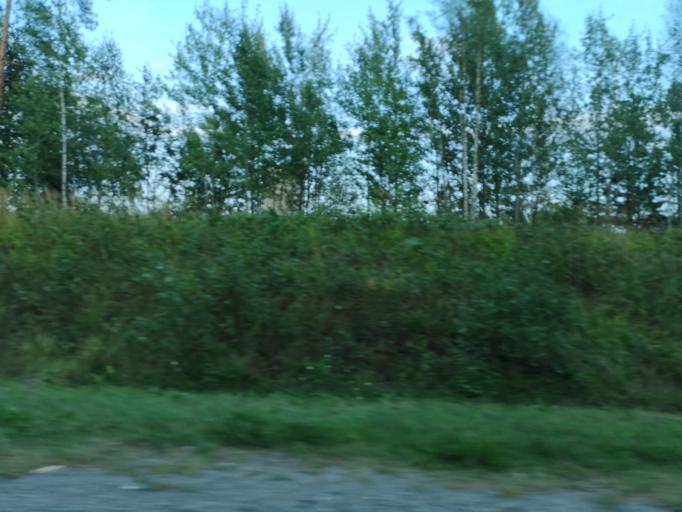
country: FI
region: Paijanne Tavastia
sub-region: Lahti
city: Hartola
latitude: 61.5474
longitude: 26.0083
